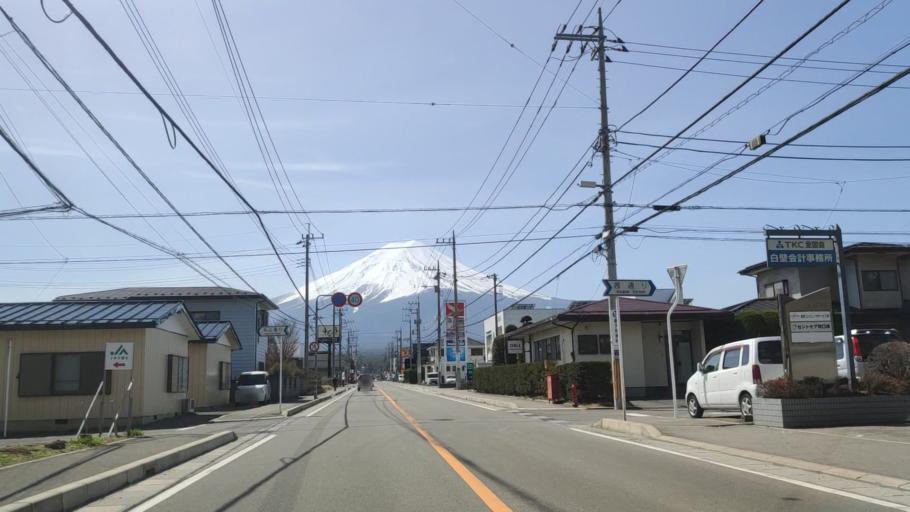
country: JP
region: Yamanashi
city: Fujikawaguchiko
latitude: 35.4943
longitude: 138.7640
